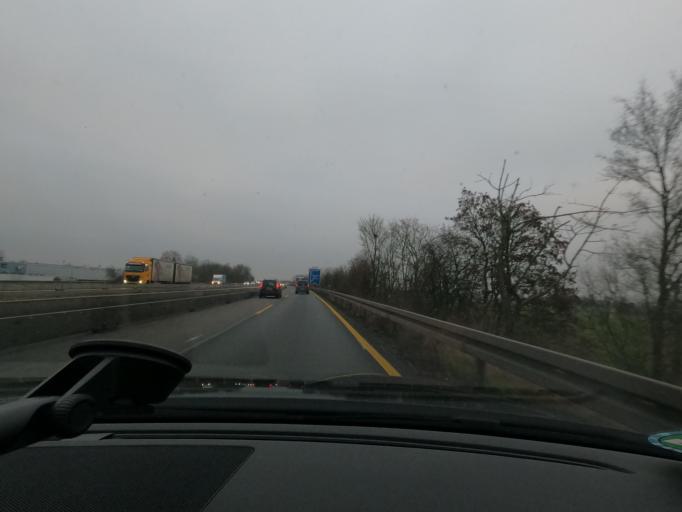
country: DE
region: North Rhine-Westphalia
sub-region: Regierungsbezirk Dusseldorf
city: Willich
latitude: 51.2794
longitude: 6.5096
